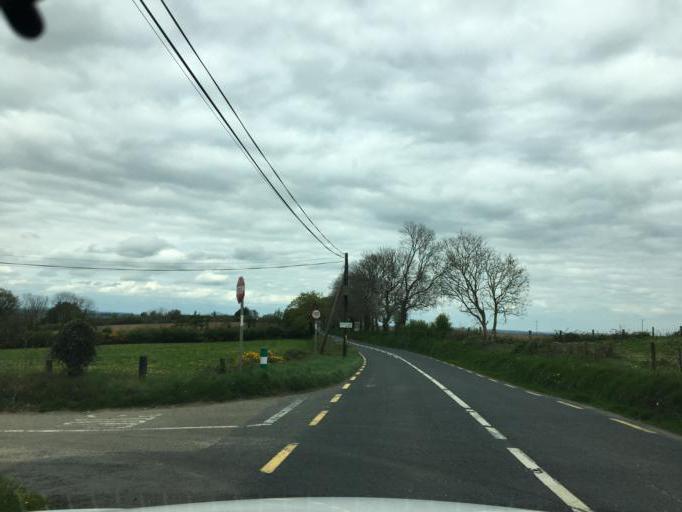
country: IE
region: Leinster
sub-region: Loch Garman
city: Enniscorthy
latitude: 52.4424
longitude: -6.7315
